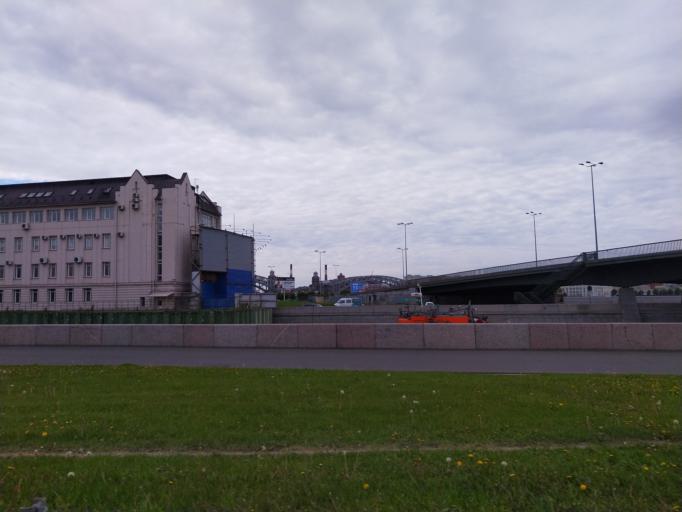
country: RU
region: Leningrad
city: Finlyandskiy
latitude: 59.9465
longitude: 30.4074
